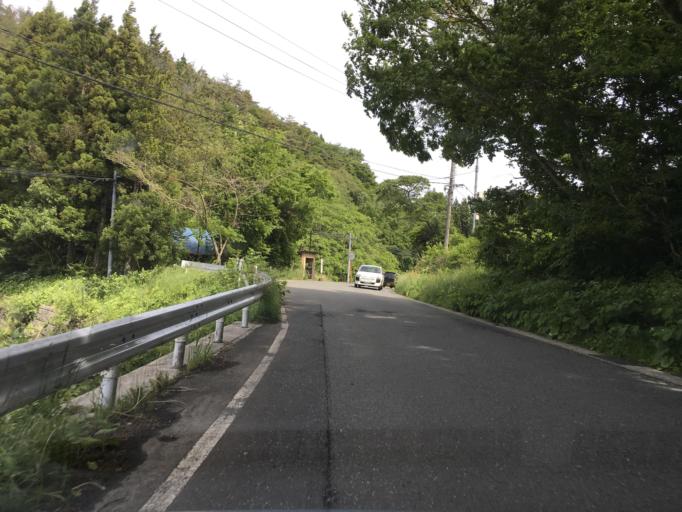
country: JP
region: Iwate
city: Mizusawa
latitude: 39.0859
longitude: 141.3510
